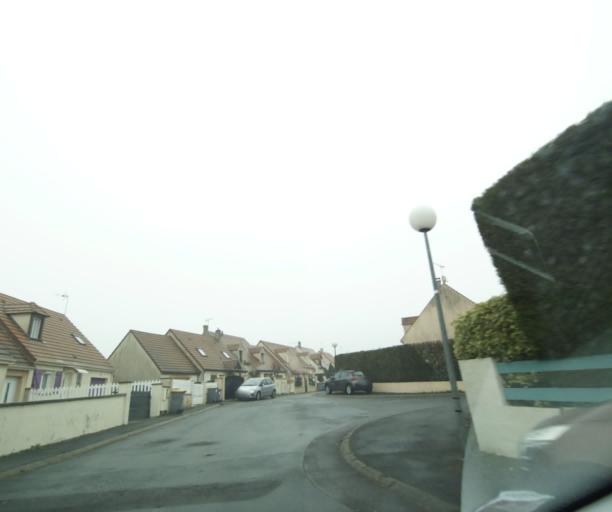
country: FR
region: Ile-de-France
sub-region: Departement de Seine-et-Marne
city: Othis
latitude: 49.0663
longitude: 2.6834
